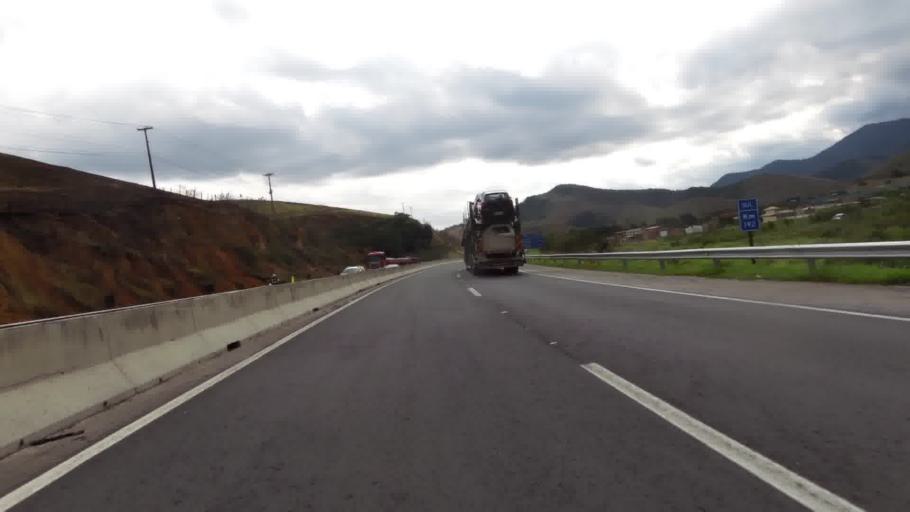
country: BR
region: Rio de Janeiro
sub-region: Casimiro De Abreu
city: Casimiro de Abreu
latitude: -22.4732
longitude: -42.0820
